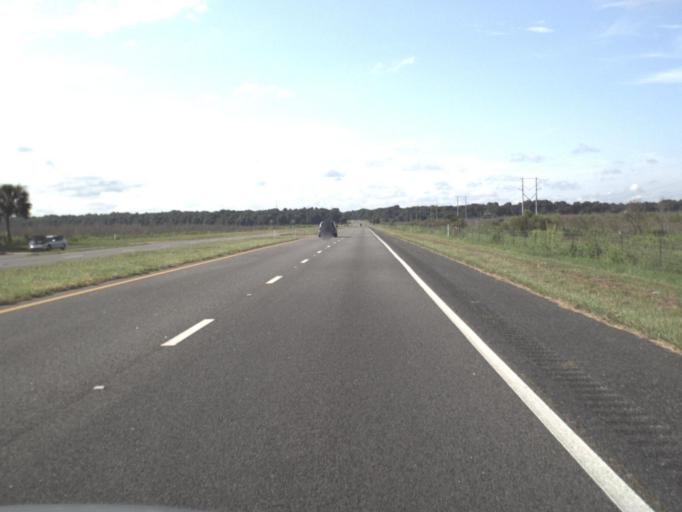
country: US
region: Florida
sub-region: Alachua County
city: Gainesville
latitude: 29.5748
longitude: -82.3355
